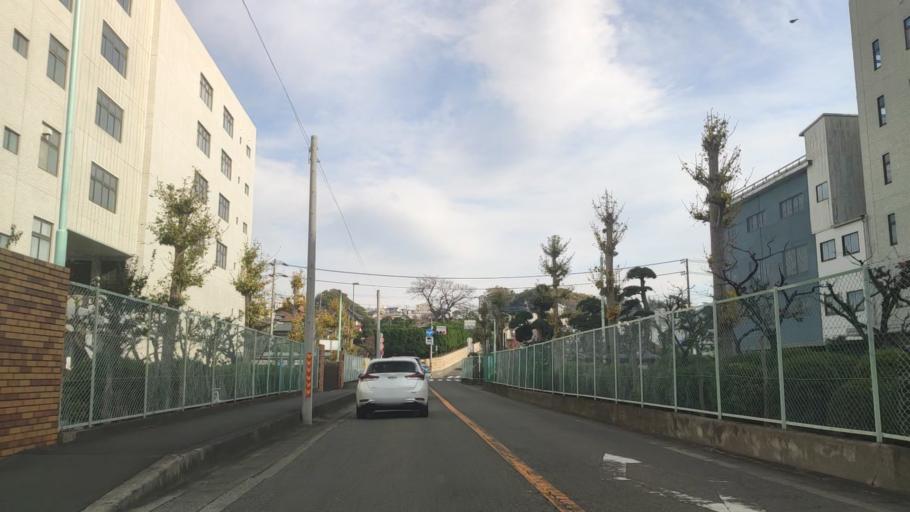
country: JP
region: Kanagawa
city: Atsugi
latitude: 35.4434
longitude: 139.3939
